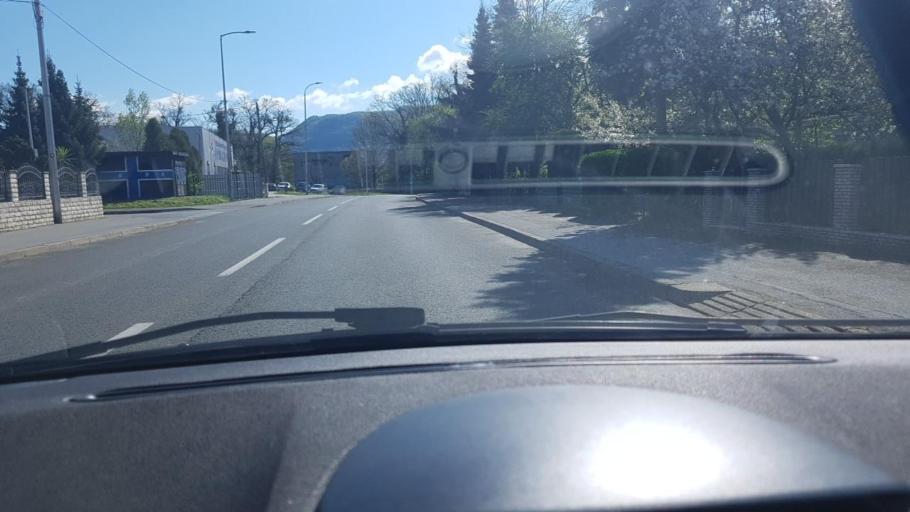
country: HR
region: Zagrebacka
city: Zapresic
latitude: 45.8693
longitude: 15.8013
